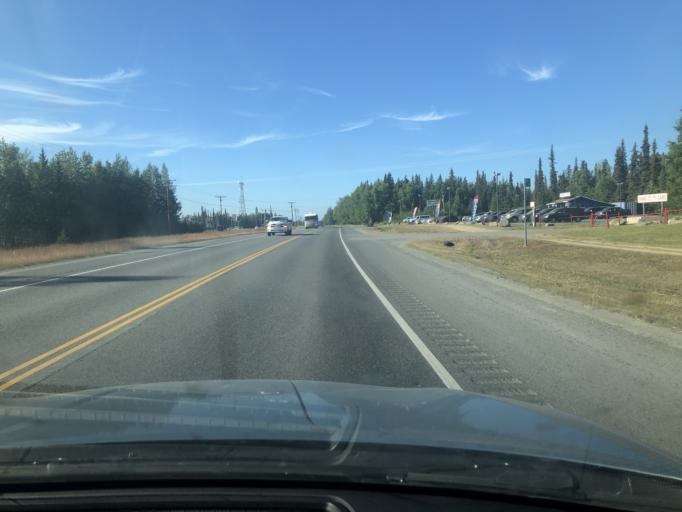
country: US
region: Alaska
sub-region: Kenai Peninsula Borough
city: Ridgeway
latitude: 60.5222
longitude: -151.0813
